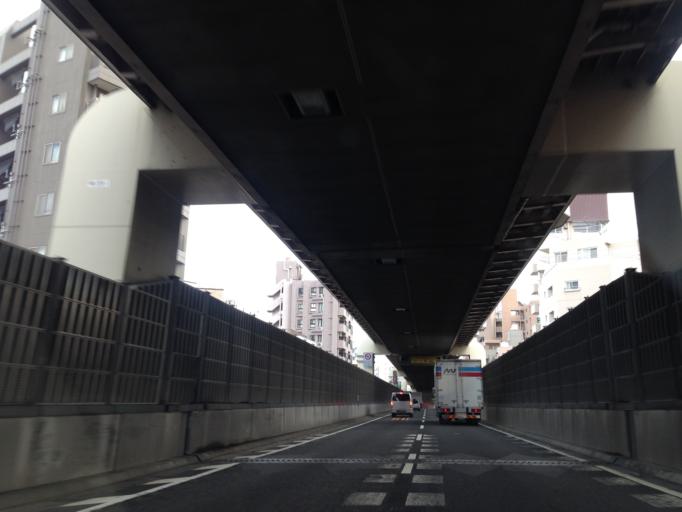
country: JP
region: Saitama
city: Kawaguchi
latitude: 35.7456
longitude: 139.7300
